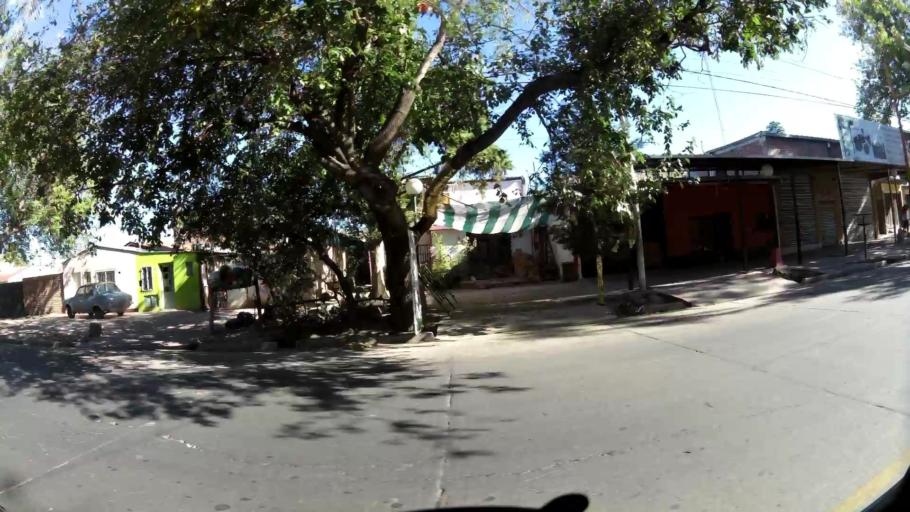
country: AR
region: Mendoza
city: Las Heras
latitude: -32.8420
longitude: -68.8303
